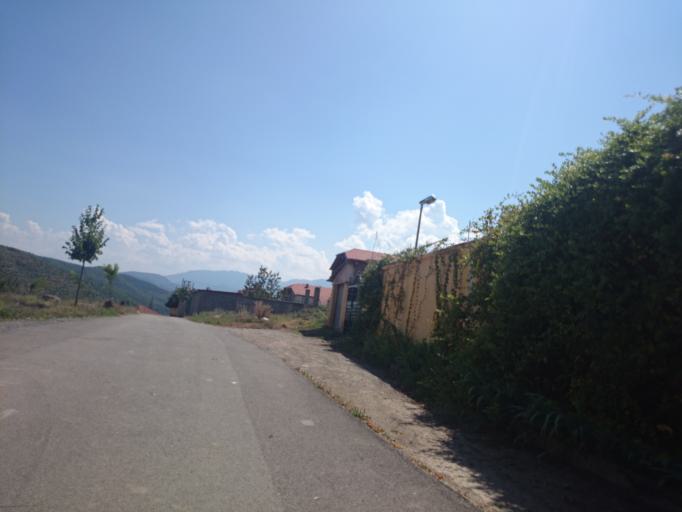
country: AL
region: Diber
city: Peshkopi
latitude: 41.6814
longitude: 20.4241
